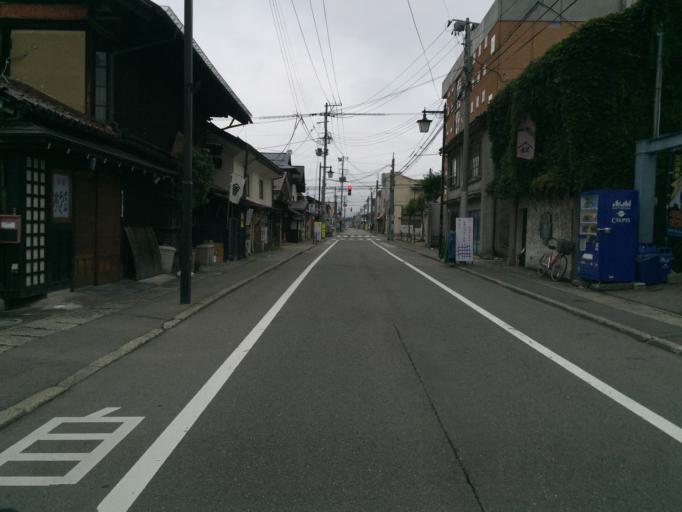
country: JP
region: Fukushima
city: Kitakata
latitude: 37.4964
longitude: 139.9337
